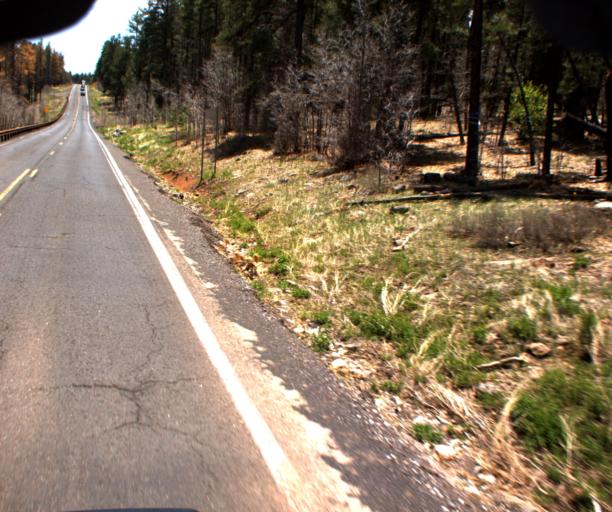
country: US
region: Arizona
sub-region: Coconino County
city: Kachina Village
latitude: 35.0511
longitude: -111.7329
